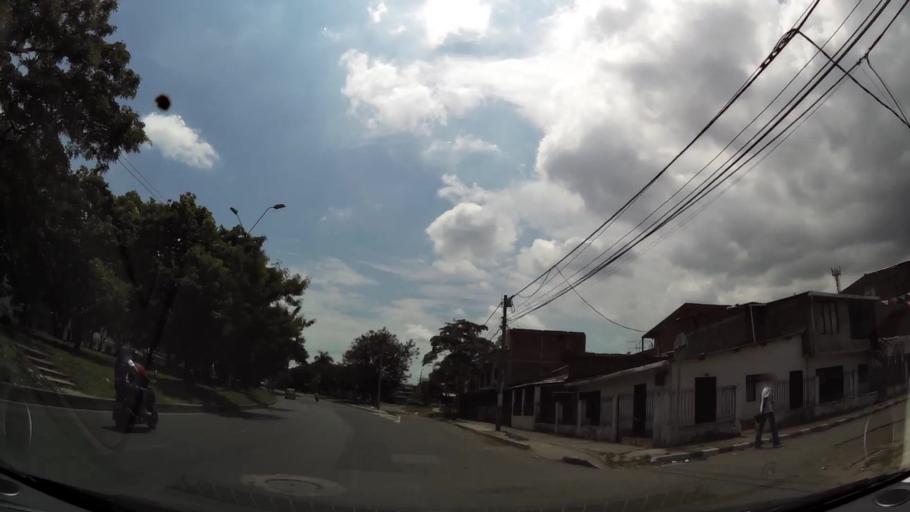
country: CO
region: Valle del Cauca
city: Cali
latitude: 3.4725
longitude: -76.4825
